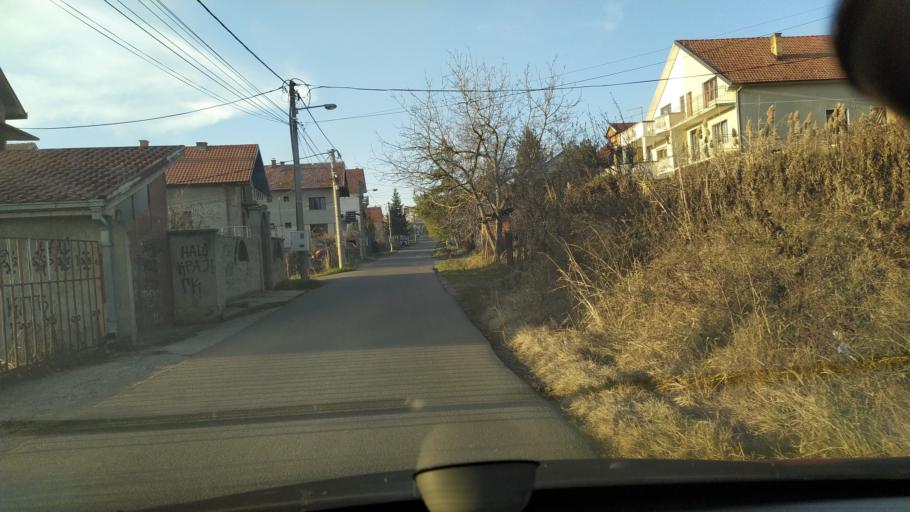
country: RS
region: Central Serbia
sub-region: Belgrade
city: Zvezdara
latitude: 44.7520
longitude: 20.5715
